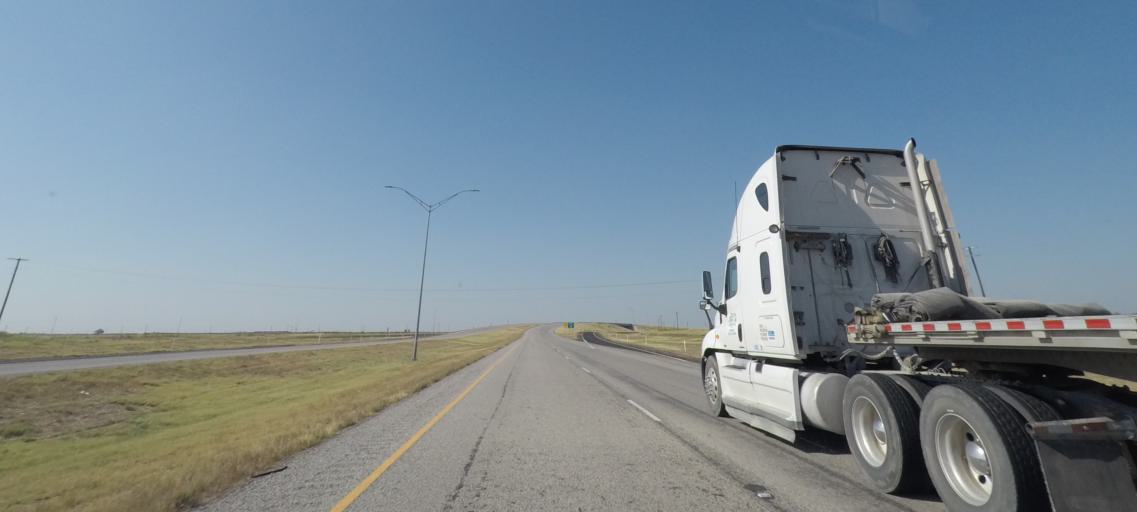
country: US
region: Texas
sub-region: Baylor County
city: Seymour
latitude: 33.6096
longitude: -99.2428
